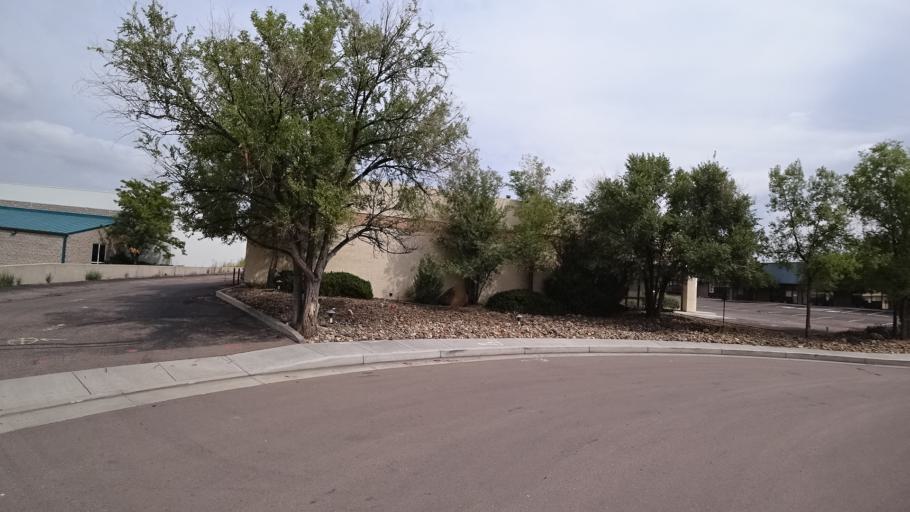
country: US
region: Colorado
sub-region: El Paso County
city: Colorado Springs
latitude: 38.8800
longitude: -104.8249
